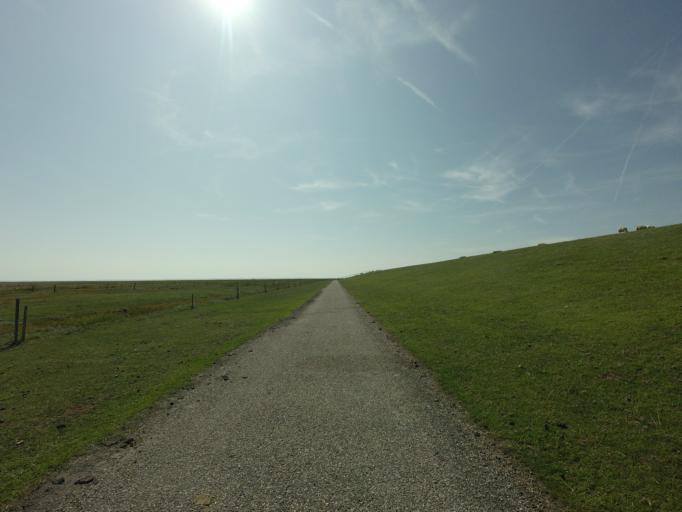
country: NL
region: Friesland
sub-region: Gemeente Schiermonnikoog
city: Schiermonnikoog
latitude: 53.4779
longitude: 6.2103
